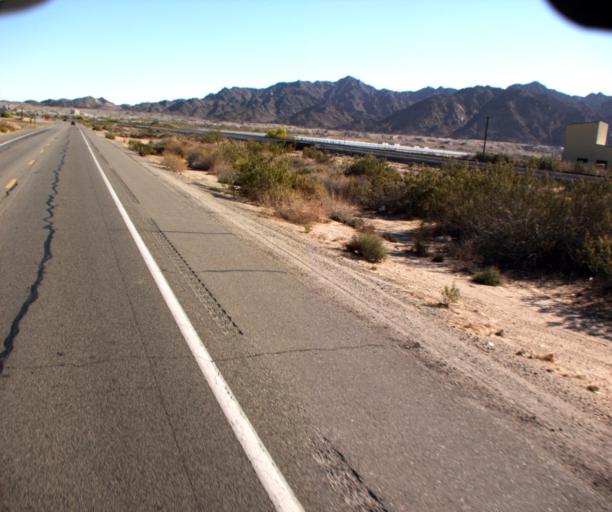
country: US
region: Arizona
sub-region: Yuma County
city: Fortuna Foothills
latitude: 32.7157
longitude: -114.4254
